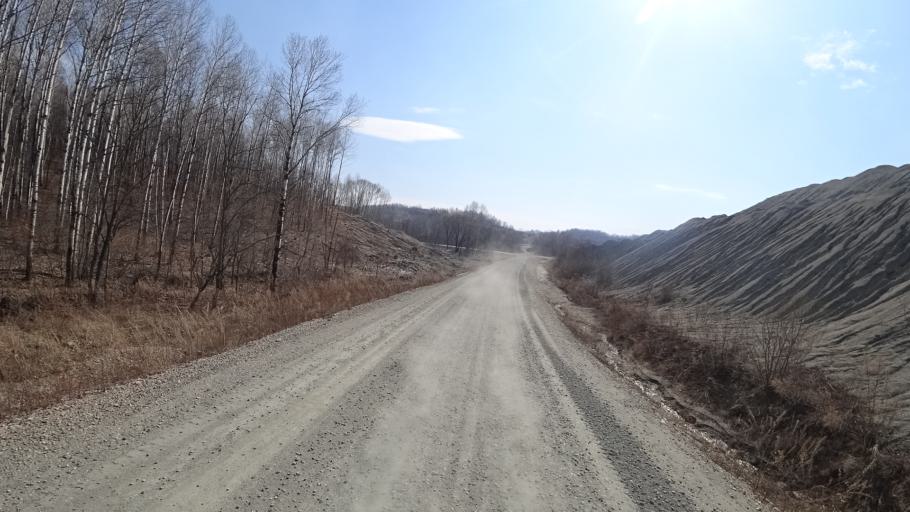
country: RU
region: Amur
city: Novobureyskiy
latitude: 49.7982
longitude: 129.9581
